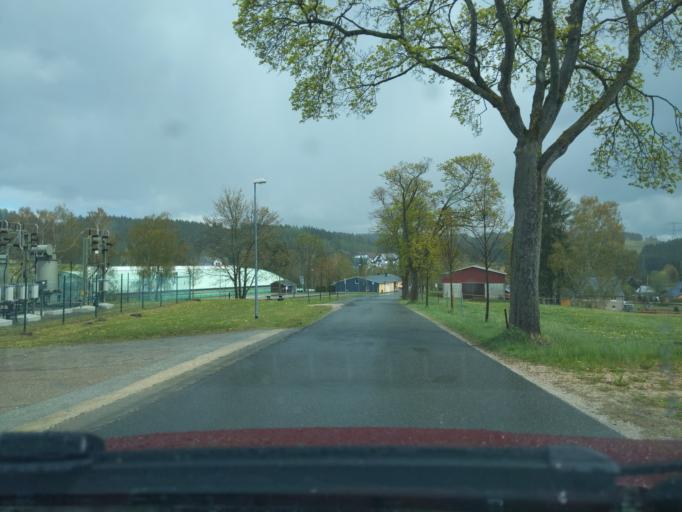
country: DE
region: Saxony
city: Schoenheide
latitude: 50.5144
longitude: 12.5245
